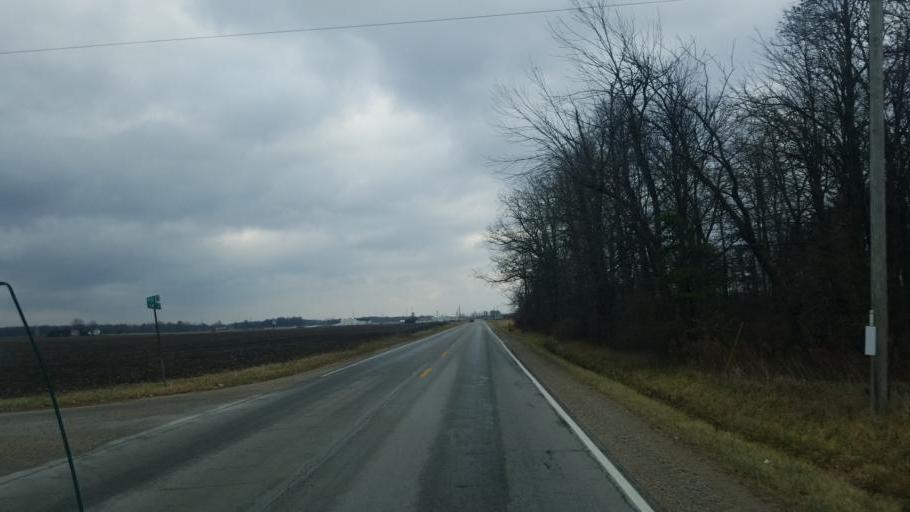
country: US
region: Indiana
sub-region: Adams County
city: Geneva
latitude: 40.5409
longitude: -84.9725
